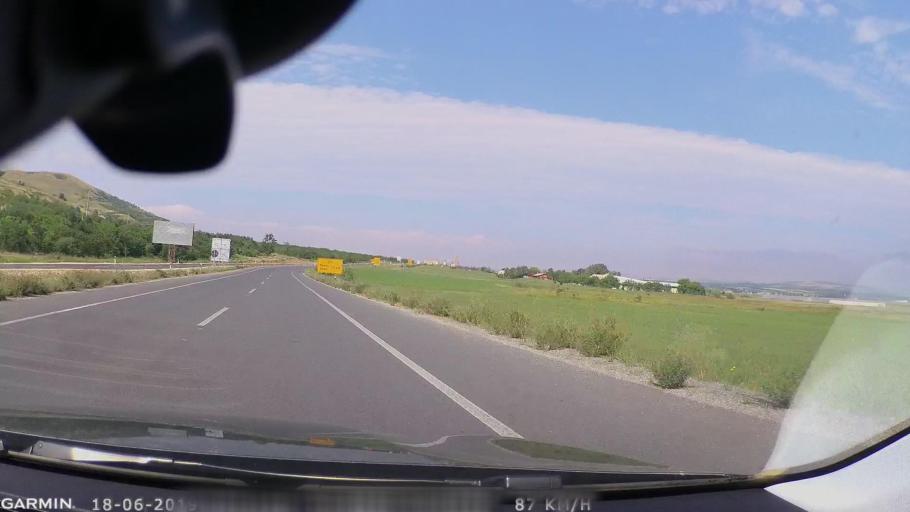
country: MK
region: Sveti Nikole
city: Sveti Nikole
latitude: 41.8275
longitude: 22.0045
